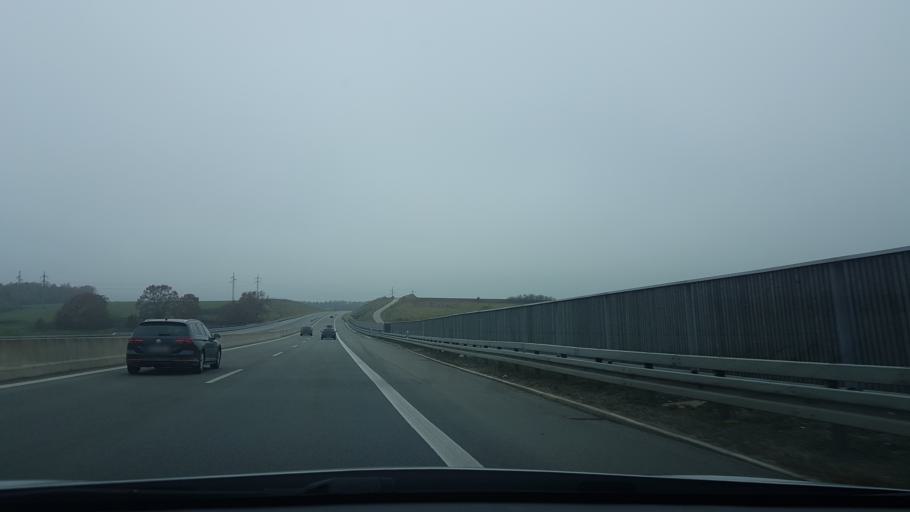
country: DE
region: Bavaria
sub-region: Lower Bavaria
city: Ergoldsbach
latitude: 48.6850
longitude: 12.1862
